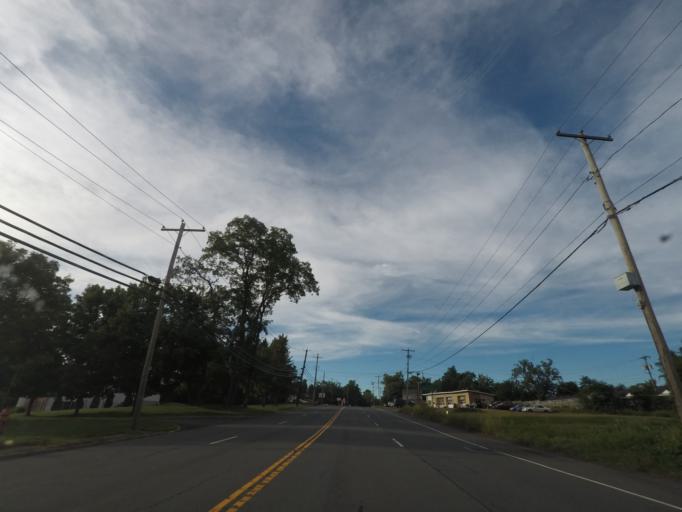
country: US
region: New York
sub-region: Rensselaer County
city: East Greenbush
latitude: 42.5728
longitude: -73.6877
